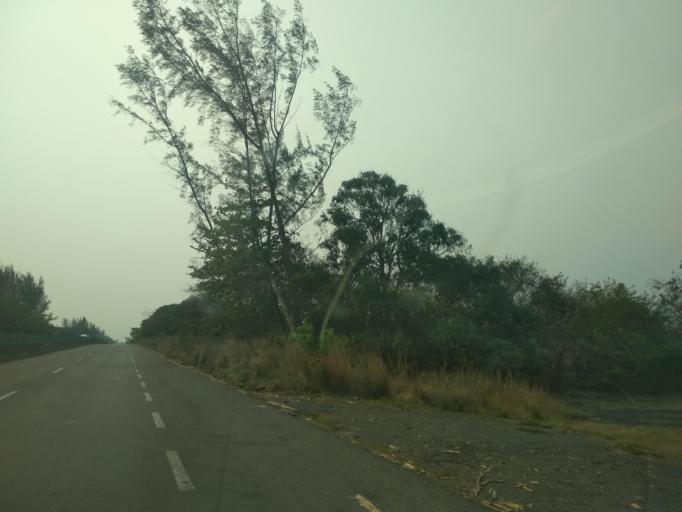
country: MX
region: Veracruz
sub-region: Veracruz
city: Las Amapolas
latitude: 19.1421
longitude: -96.2521
